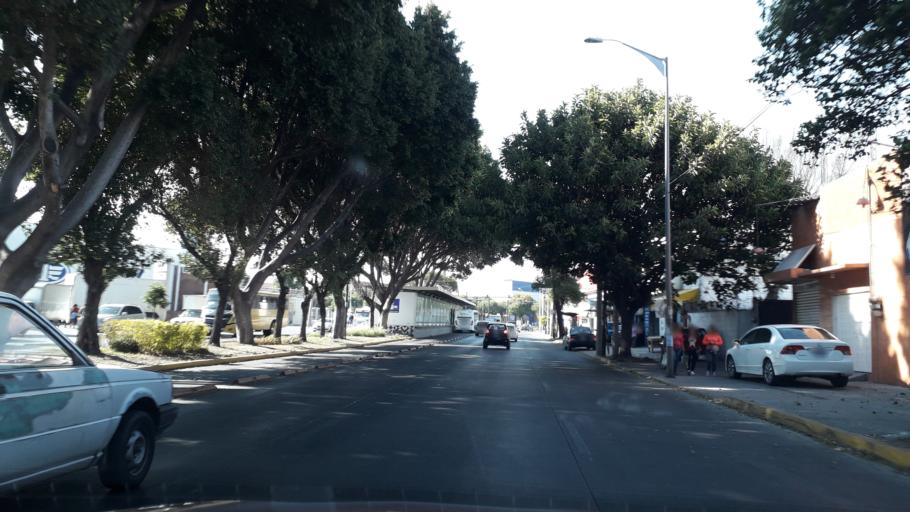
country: MX
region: Puebla
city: Puebla
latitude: 19.0674
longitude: -98.1916
